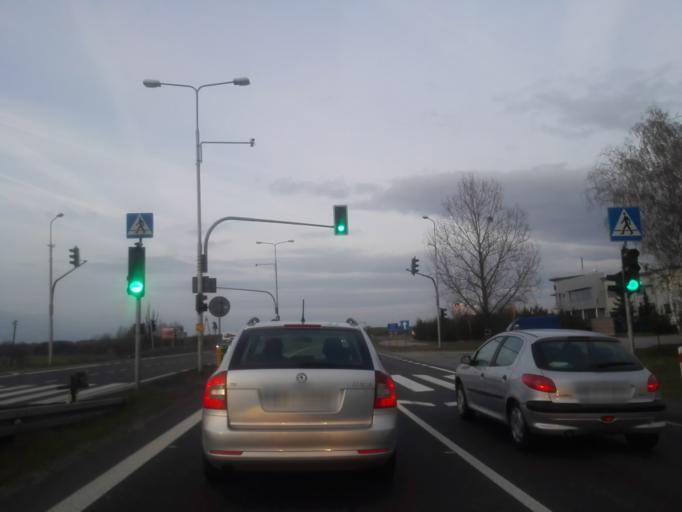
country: PL
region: Masovian Voivodeship
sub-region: Powiat zyrardowski
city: Radziejowice
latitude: 52.0095
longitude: 20.6081
